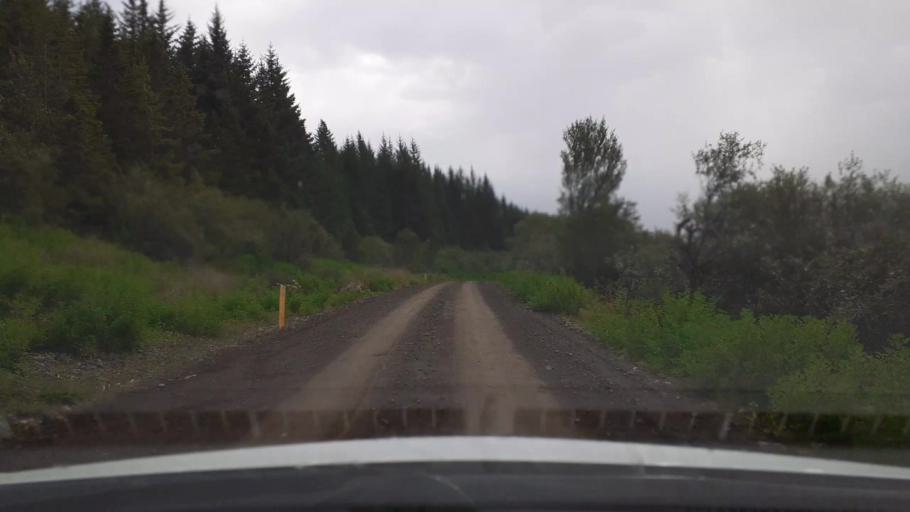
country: IS
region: Capital Region
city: Mosfellsbaer
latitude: 64.5164
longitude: -21.4169
